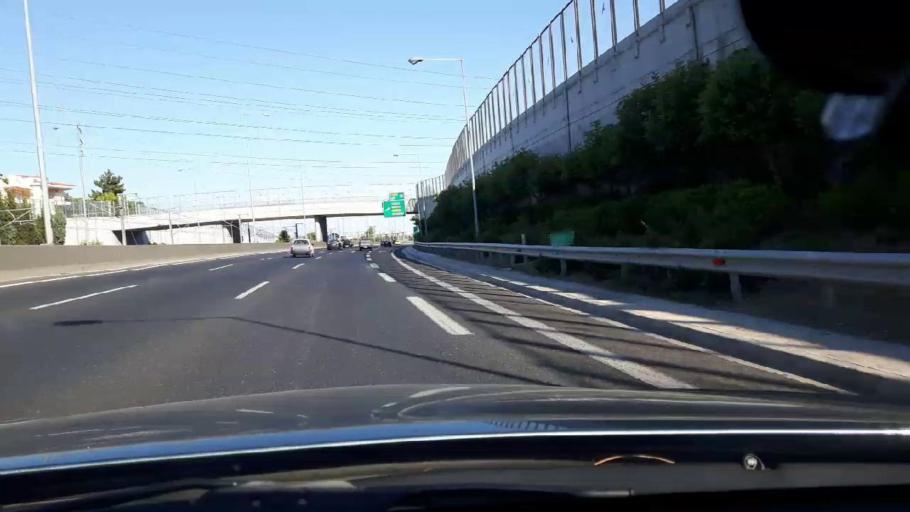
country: GR
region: Attica
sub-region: Nomarchia Anatolikis Attikis
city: Pallini
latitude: 38.0098
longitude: 23.8682
